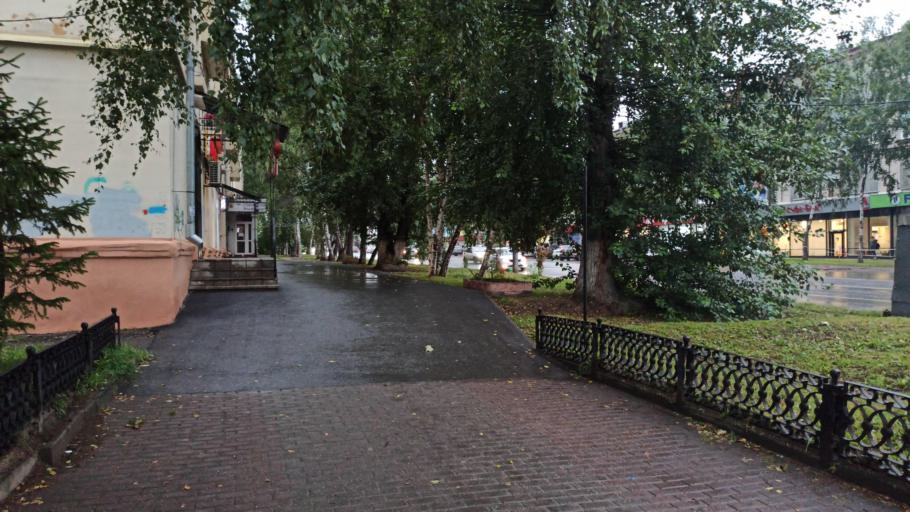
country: RU
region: Tomsk
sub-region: Tomskiy Rayon
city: Tomsk
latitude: 56.4636
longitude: 84.9659
